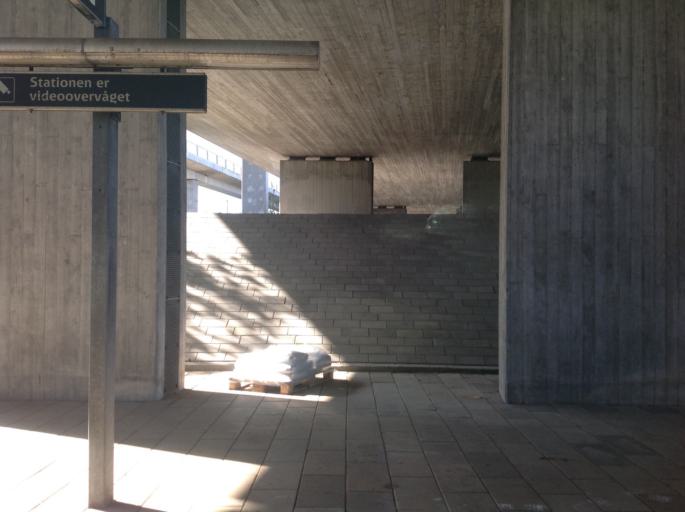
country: DK
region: Capital Region
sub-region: Tarnby Kommune
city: Tarnby
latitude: 55.6284
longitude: 12.5792
